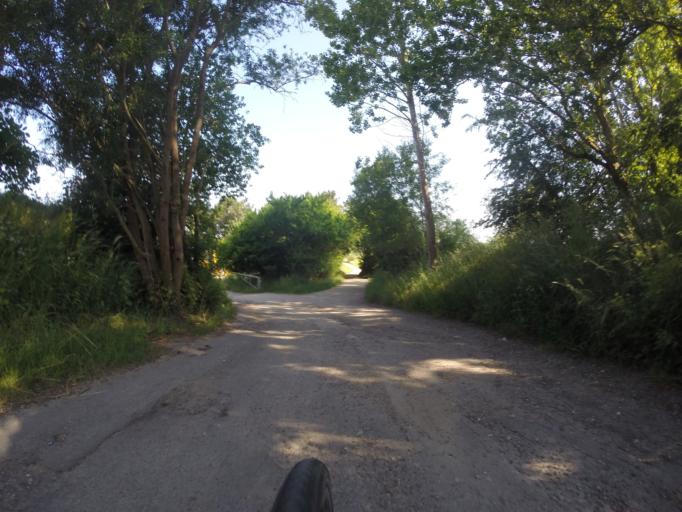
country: DK
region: Capital Region
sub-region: Herlev Kommune
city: Herlev
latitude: 55.7464
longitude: 12.4407
